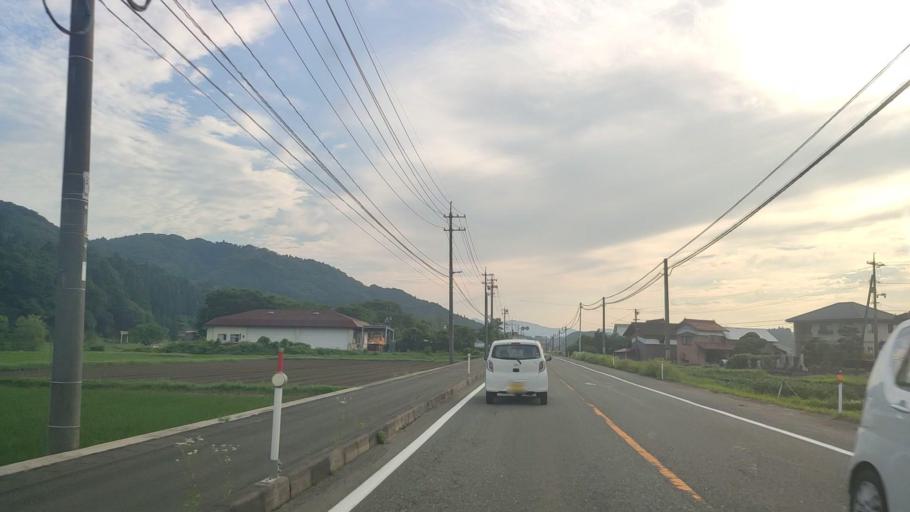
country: JP
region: Tottori
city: Kurayoshi
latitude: 35.2903
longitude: 133.7187
